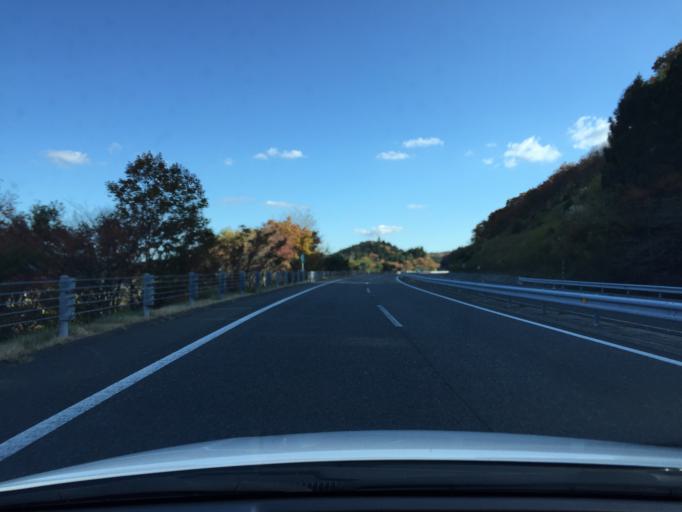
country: JP
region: Fukushima
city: Funehikimachi-funehiki
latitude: 37.2526
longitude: 140.6571
